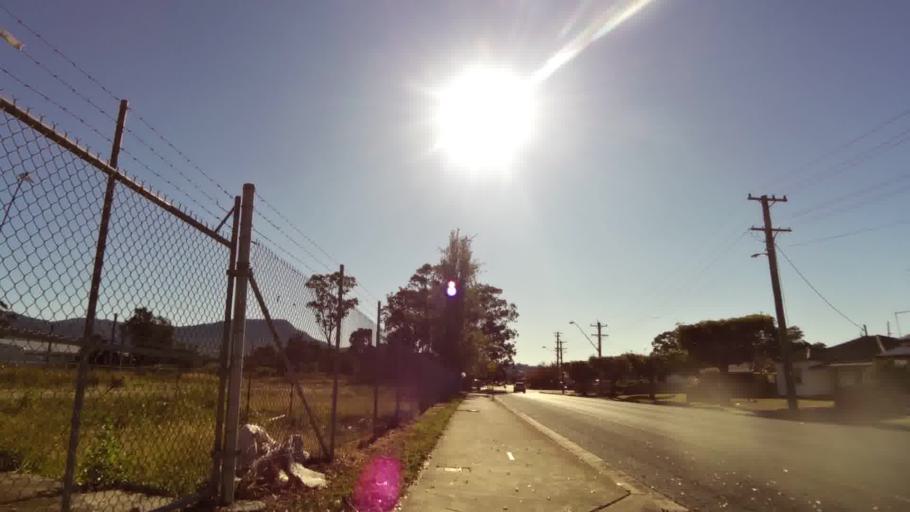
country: AU
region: New South Wales
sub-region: Wollongong
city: Dapto
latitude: -34.4906
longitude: 150.7940
